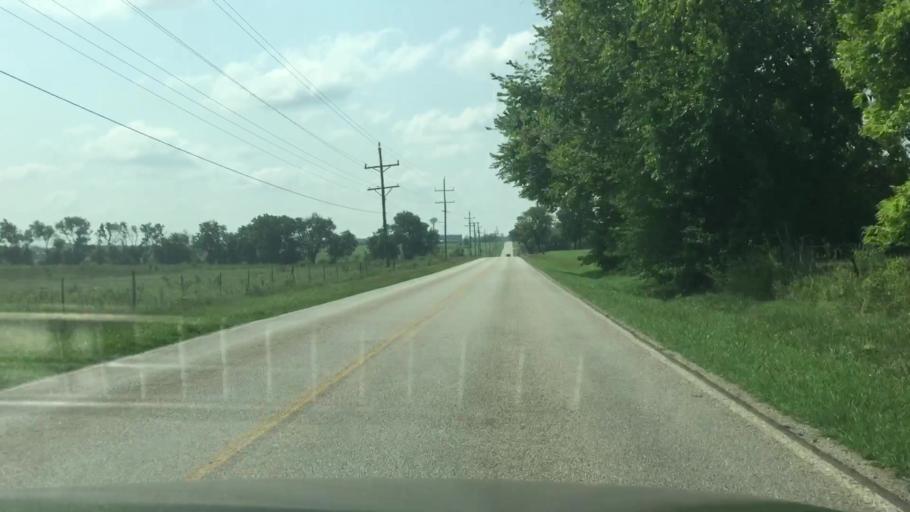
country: US
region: Kansas
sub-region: Allen County
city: Humboldt
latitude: 37.8369
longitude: -95.4368
